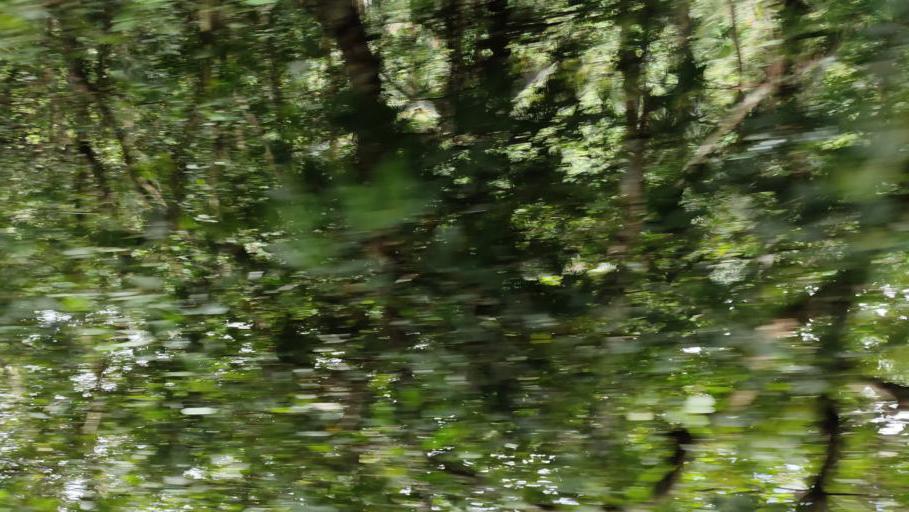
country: IN
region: Kerala
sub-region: Kasaragod District
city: Nileshwar
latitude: 12.2868
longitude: 75.2706
